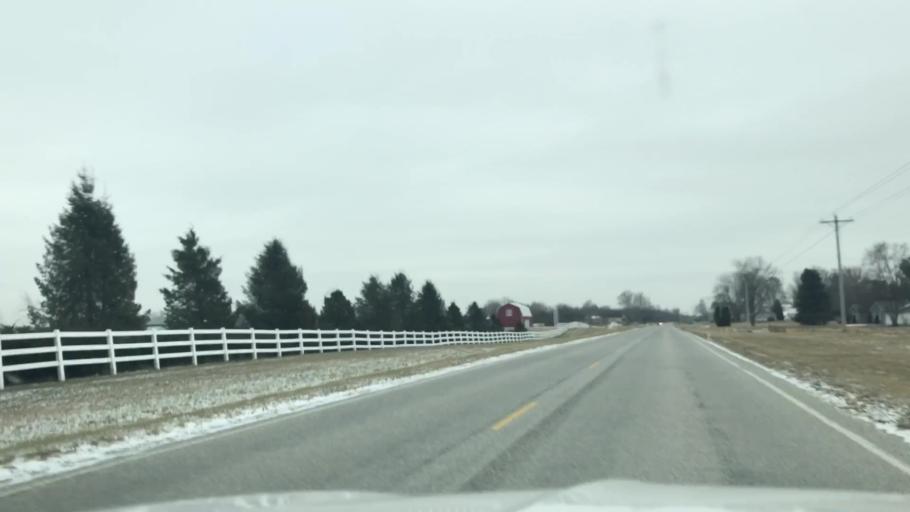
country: US
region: Indiana
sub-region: Fulton County
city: Rochester
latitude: 41.0354
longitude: -86.1994
